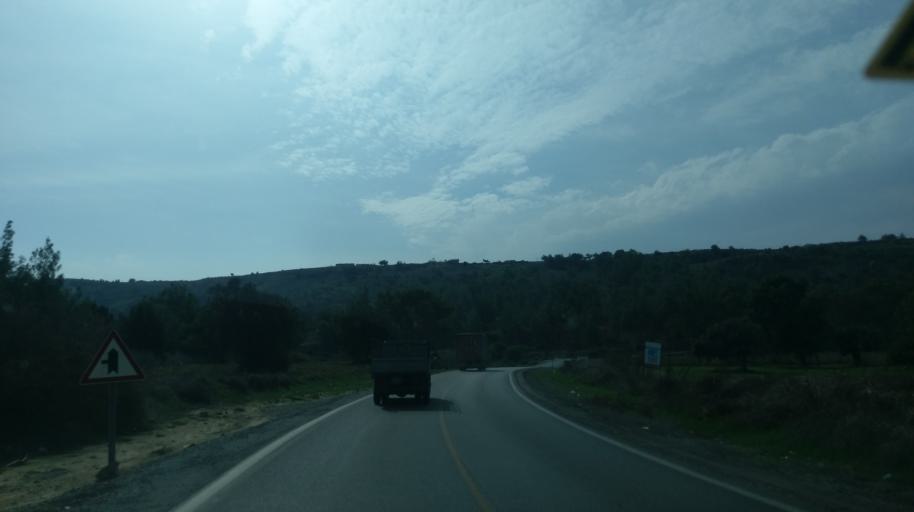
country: CY
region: Lefkosia
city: Morfou
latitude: 35.2571
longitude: 33.0415
